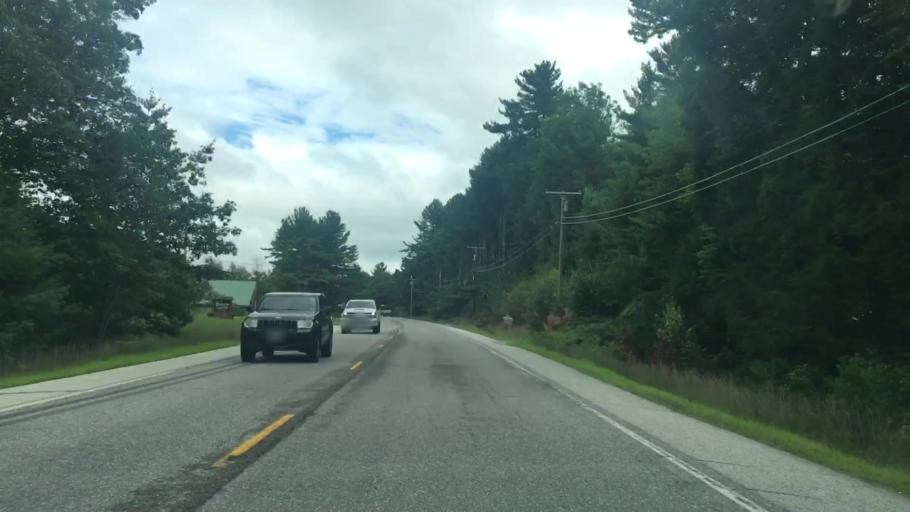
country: US
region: Maine
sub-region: York County
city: Lake Arrowhead
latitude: 43.6470
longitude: -70.7590
